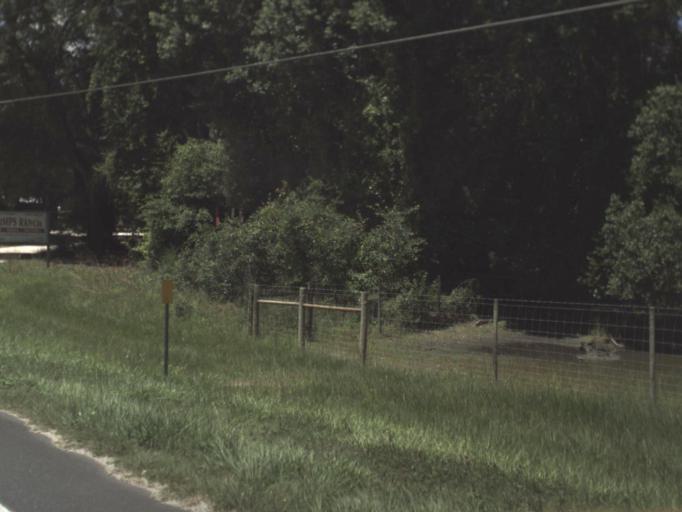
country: US
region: Florida
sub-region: Alachua County
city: Hawthorne
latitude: 29.6568
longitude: -82.0330
